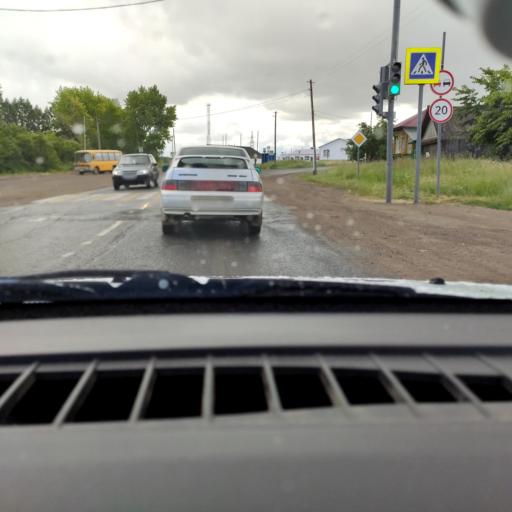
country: RU
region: Perm
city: Orda
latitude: 57.1924
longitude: 56.9042
